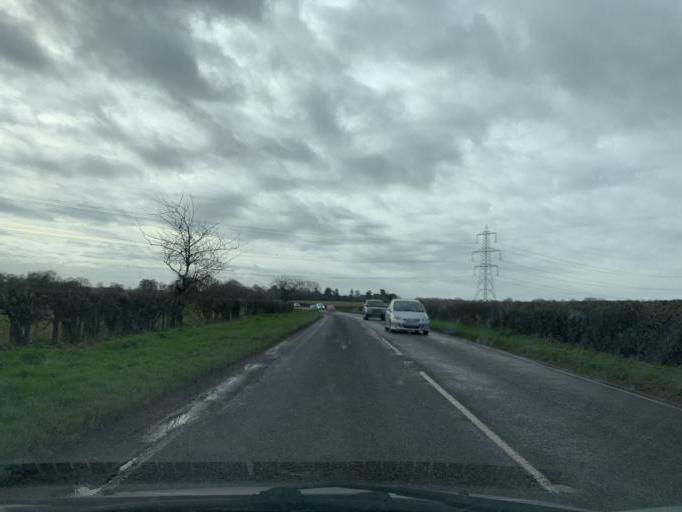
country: GB
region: England
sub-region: Hampshire
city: Fordingbridge
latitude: 50.9533
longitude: -1.7778
